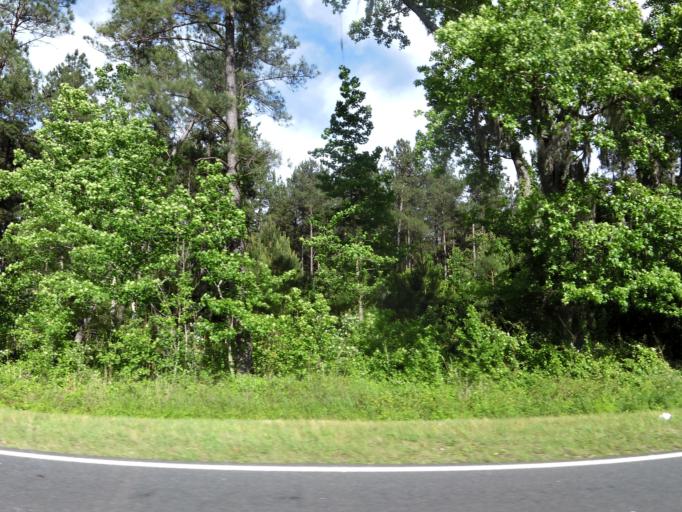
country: US
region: South Carolina
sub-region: Allendale County
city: Fairfax
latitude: 33.0020
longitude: -81.2197
